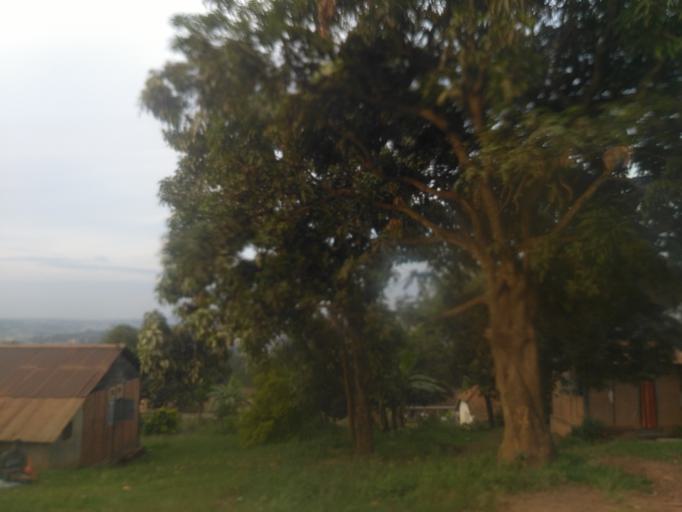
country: UG
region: Central Region
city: Kampala Central Division
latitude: 0.3414
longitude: 32.5802
